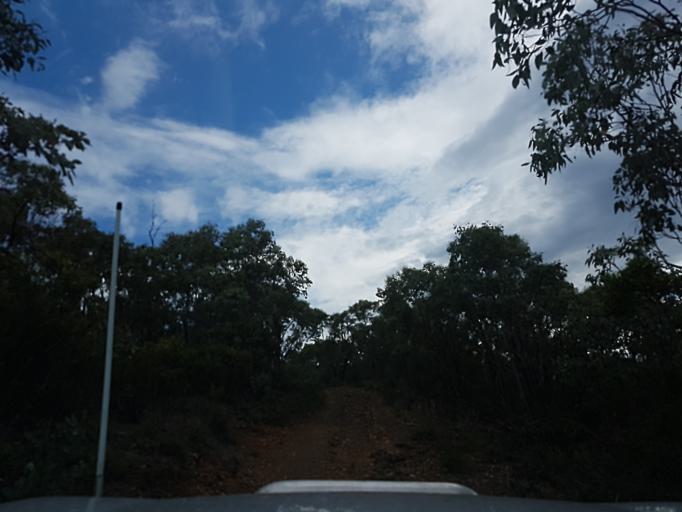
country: AU
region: New South Wales
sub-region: Snowy River
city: Jindabyne
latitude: -36.9965
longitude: 148.4059
